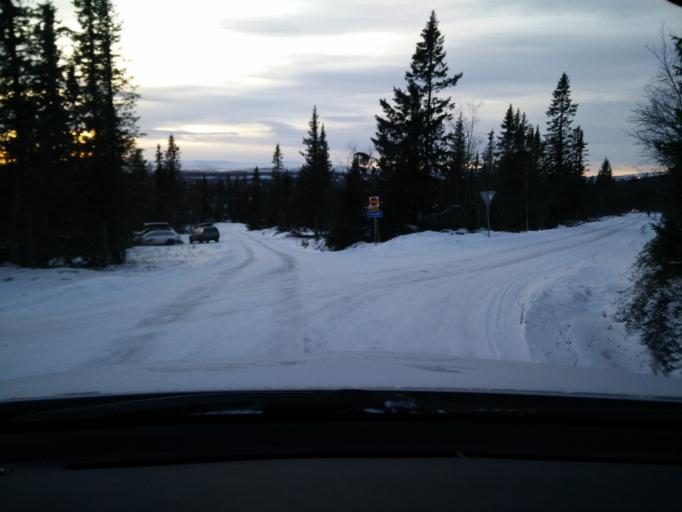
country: SE
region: Jaemtland
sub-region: Bergs Kommun
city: Hoverberg
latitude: 62.4890
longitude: 14.1428
